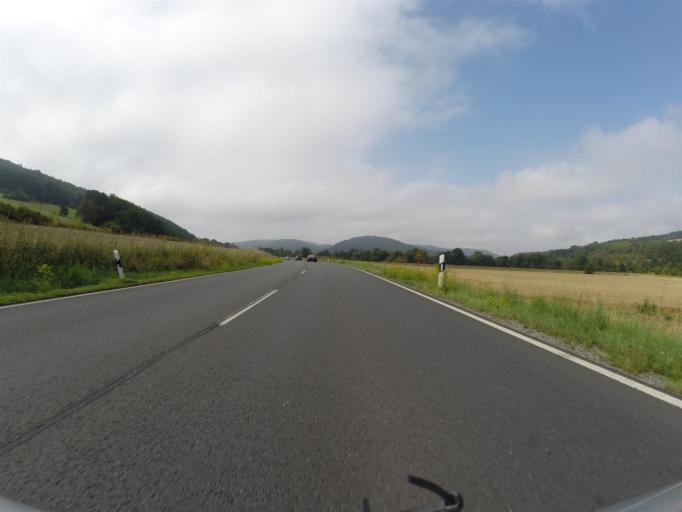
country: DE
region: Hesse
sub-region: Regierungsbezirk Kassel
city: Eschwege
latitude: 51.1428
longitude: 9.9839
